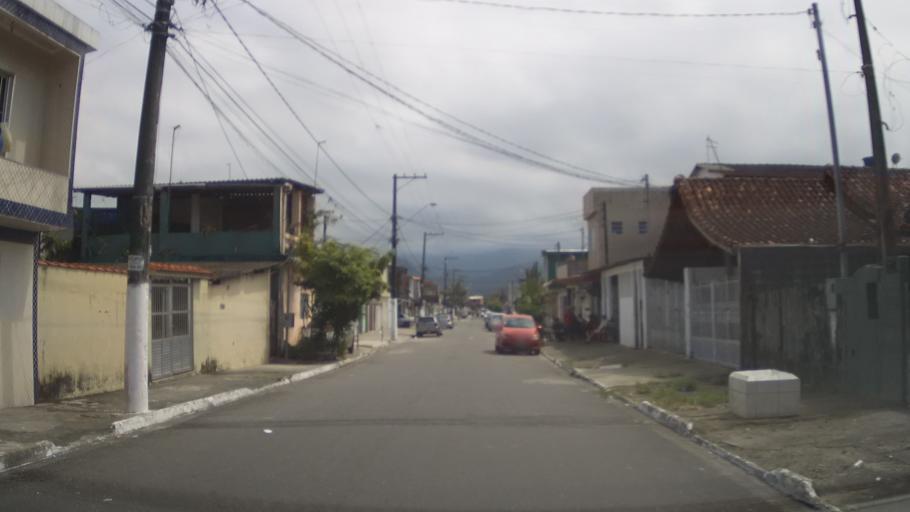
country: BR
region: Sao Paulo
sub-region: Praia Grande
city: Praia Grande
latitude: -24.0211
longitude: -46.4908
